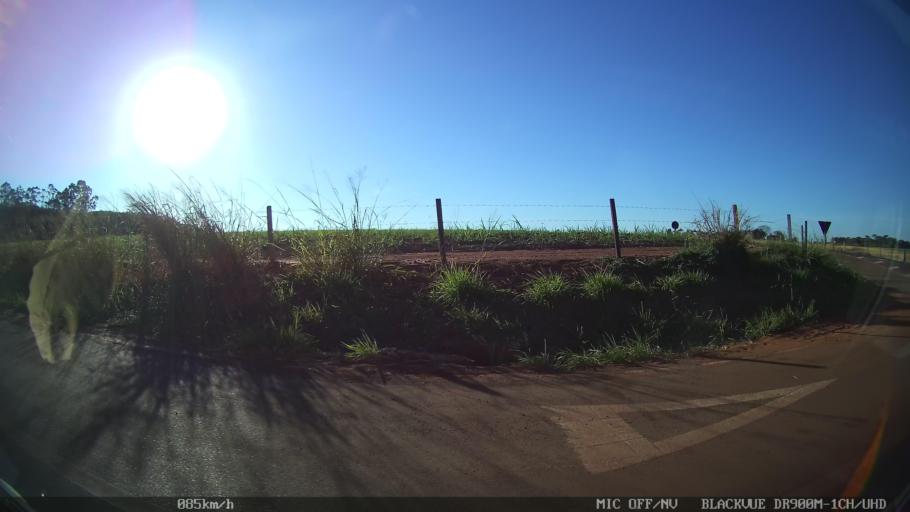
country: BR
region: Sao Paulo
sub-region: Guapiacu
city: Guapiacu
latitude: -20.7594
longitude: -49.1714
